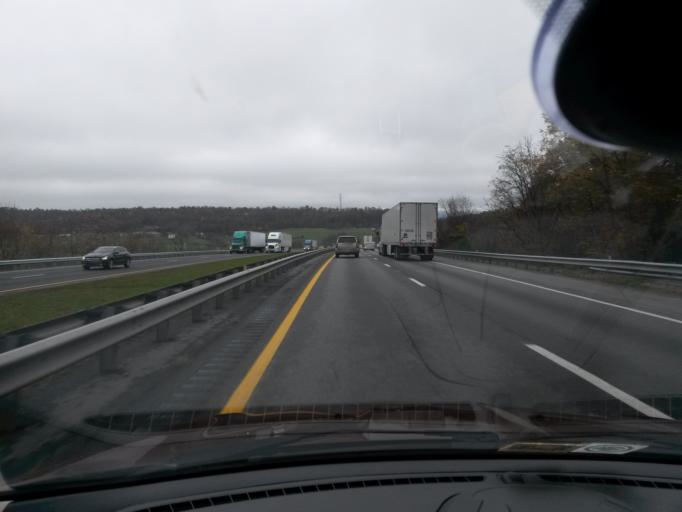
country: US
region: Virginia
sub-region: Carroll County
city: Woodlawn
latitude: 36.8843
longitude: -80.8741
